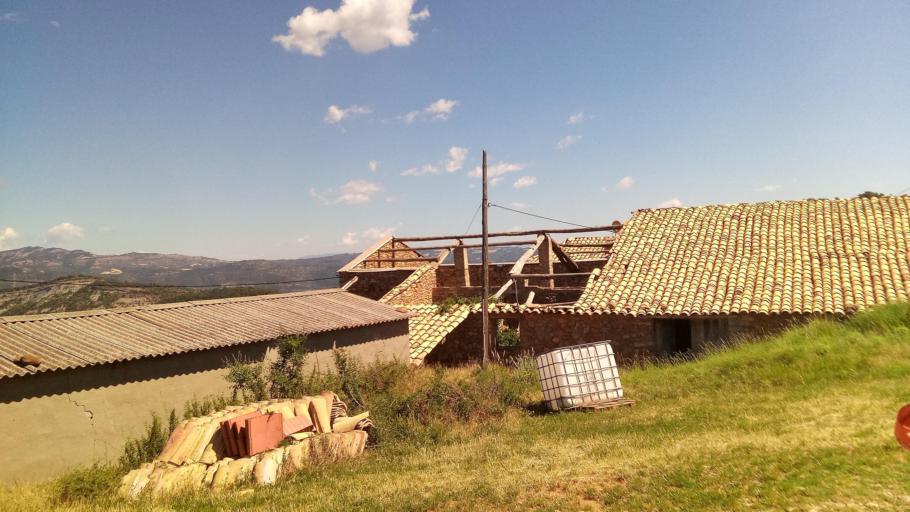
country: ES
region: Aragon
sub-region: Provincia de Huesca
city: Lascuarre
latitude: 42.3155
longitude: 0.4924
